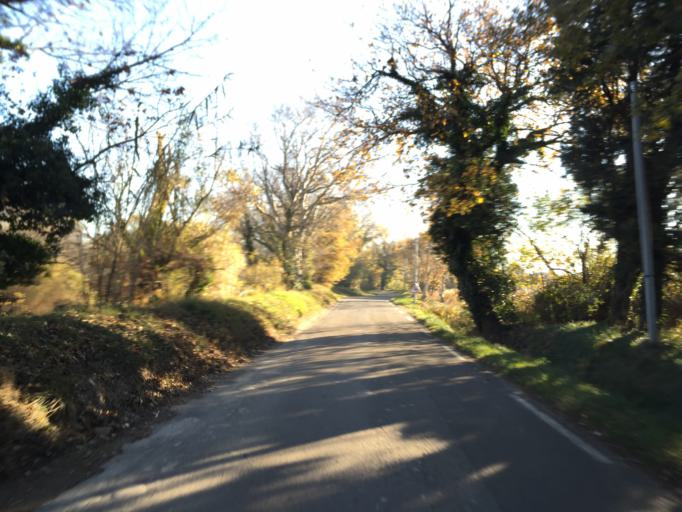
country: FR
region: Provence-Alpes-Cote d'Azur
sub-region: Departement du Vaucluse
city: Bedarrides
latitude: 44.0390
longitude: 4.9136
